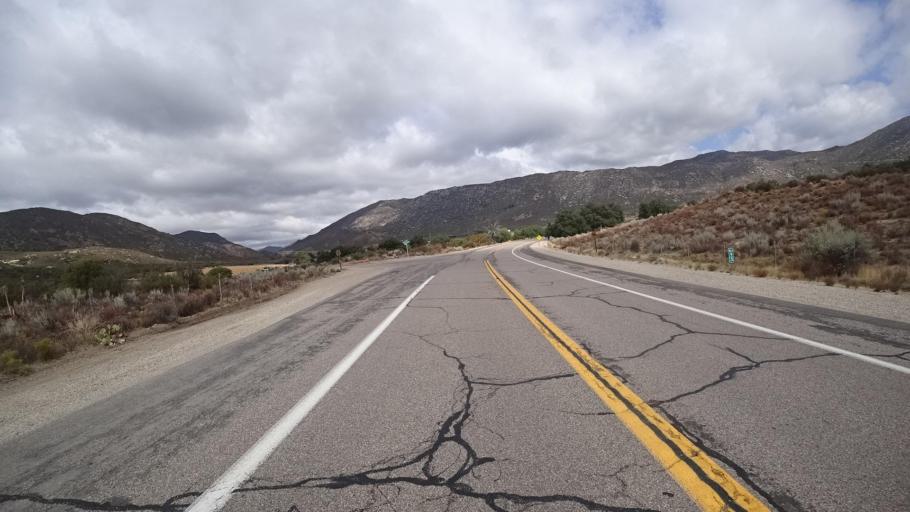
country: US
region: California
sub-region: San Diego County
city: Pine Valley
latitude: 32.7569
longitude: -116.4930
